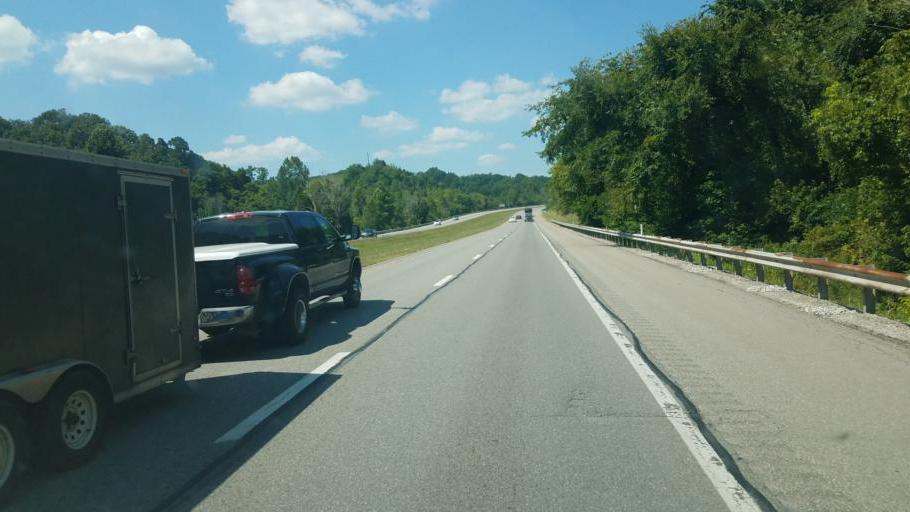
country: US
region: West Virginia
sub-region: Kanawha County
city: Sissonville
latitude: 38.5290
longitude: -81.6446
